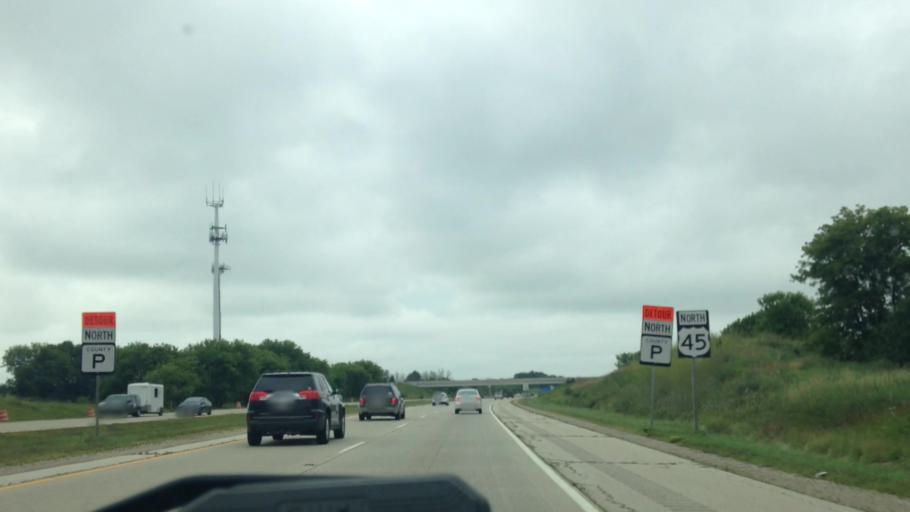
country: US
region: Wisconsin
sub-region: Washington County
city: Jackson
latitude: 43.3351
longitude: -88.1899
